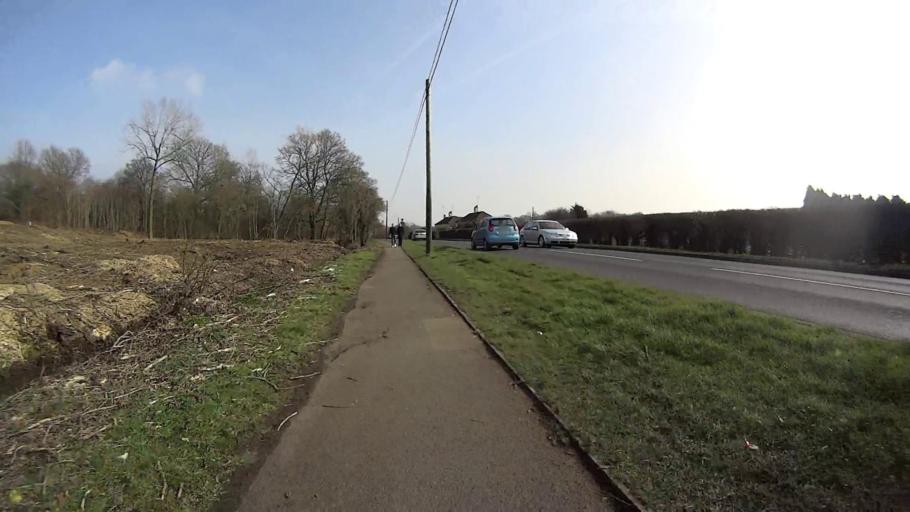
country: GB
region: England
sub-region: Surrey
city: Salfords
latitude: 51.2198
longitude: -0.1843
